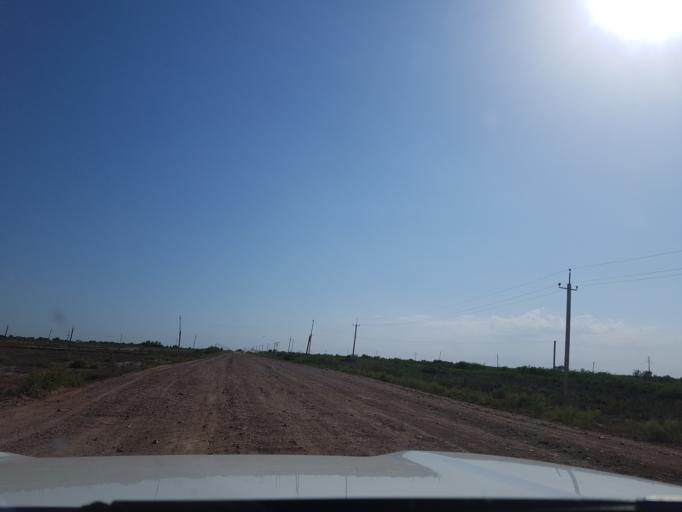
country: TM
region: Dasoguz
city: Koeneuergench
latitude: 42.0617
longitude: 58.8465
